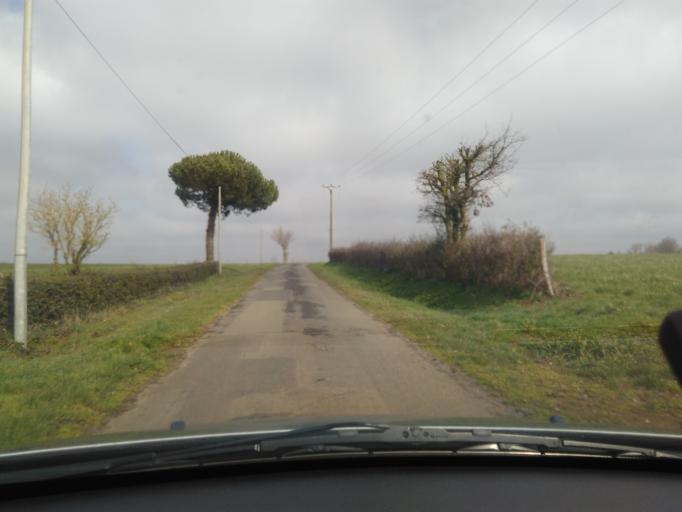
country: FR
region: Pays de la Loire
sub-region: Departement de la Vendee
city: Sainte-Cecile
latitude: 46.7057
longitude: -1.1354
